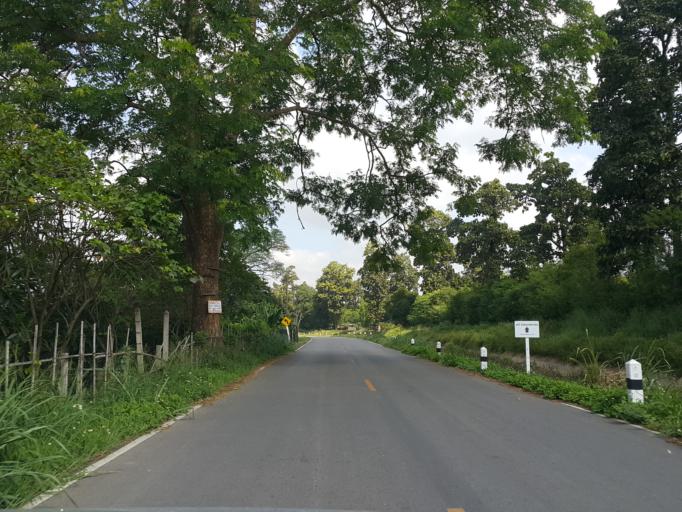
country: TH
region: Chiang Mai
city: San Sai
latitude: 18.8946
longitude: 99.0226
